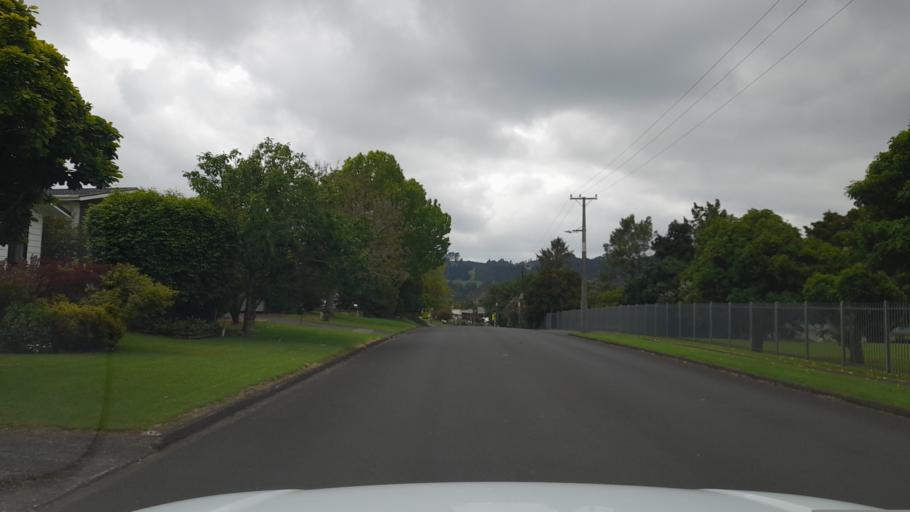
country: NZ
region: Northland
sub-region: Far North District
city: Waimate North
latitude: -35.4075
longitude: 173.7906
